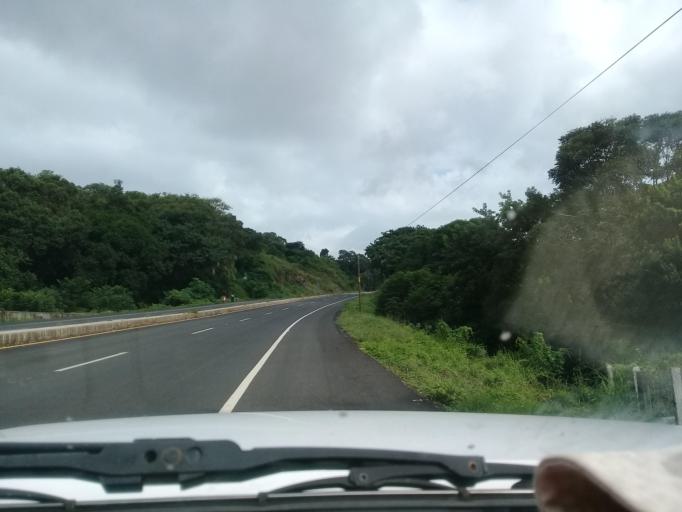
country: MX
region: Veracruz
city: Catemaco
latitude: 18.4308
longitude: -95.1295
